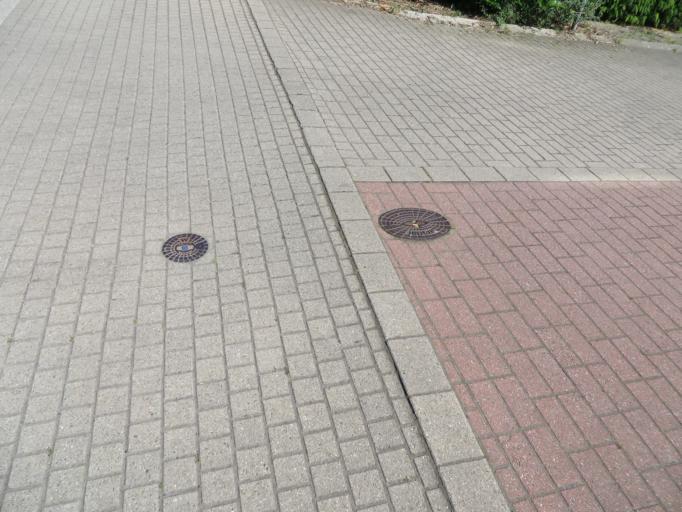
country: DE
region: North Rhine-Westphalia
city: Witten
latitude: 51.4566
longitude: 7.3501
